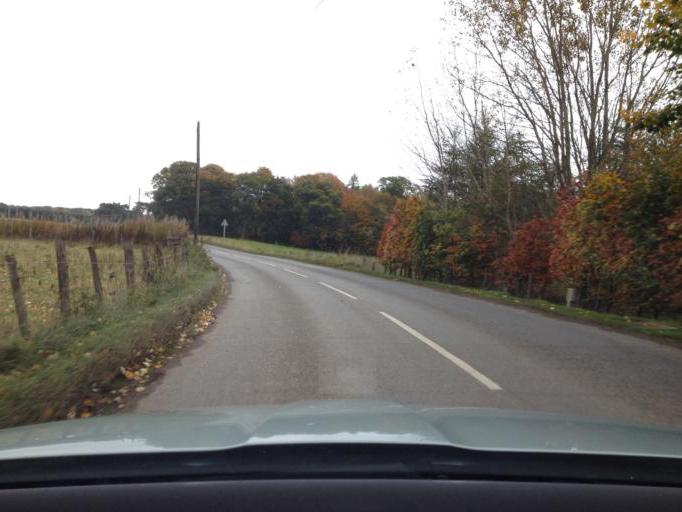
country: GB
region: Scotland
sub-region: Perth and Kinross
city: Stanley
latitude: 56.5130
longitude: -3.4092
